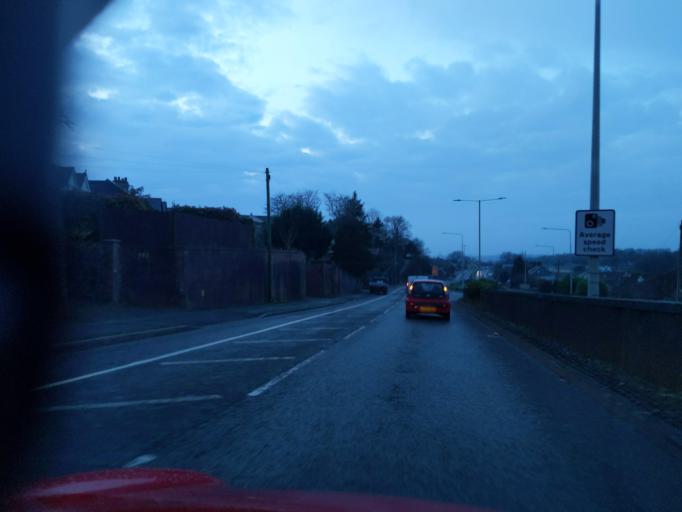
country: GB
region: England
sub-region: Plymouth
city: Plymstock
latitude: 50.3626
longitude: -4.0707
